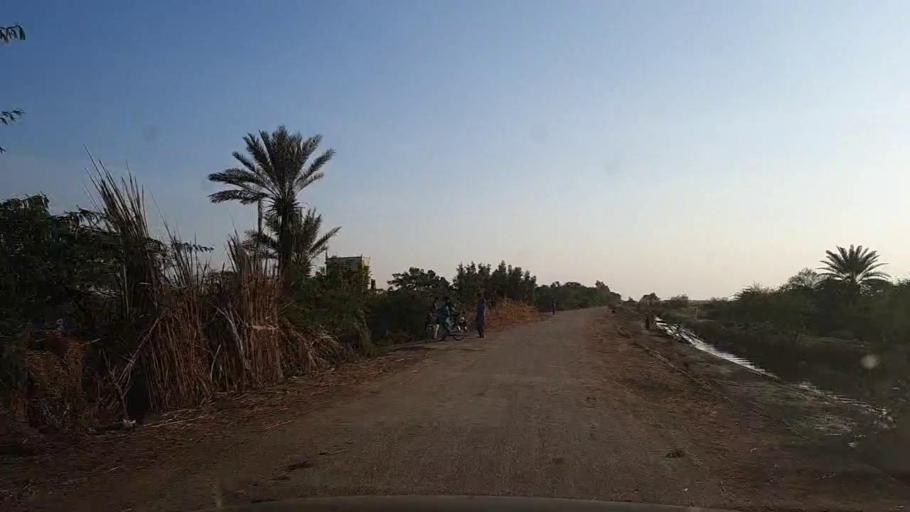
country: PK
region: Sindh
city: Thatta
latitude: 24.6213
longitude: 67.9136
